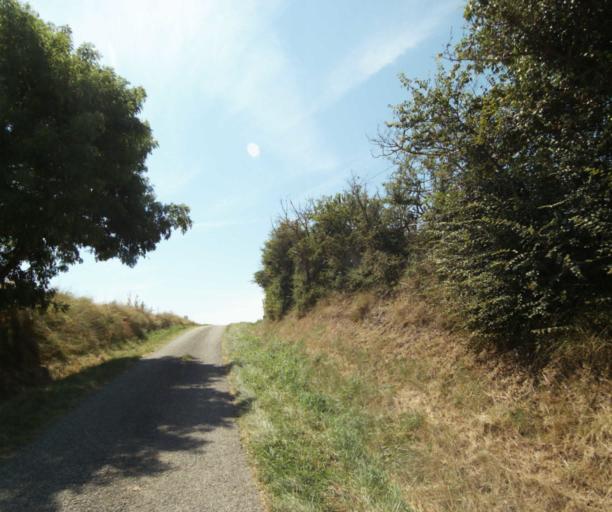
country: FR
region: Midi-Pyrenees
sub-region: Departement de l'Ariege
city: Lezat-sur-Leze
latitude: 43.2659
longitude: 1.3229
